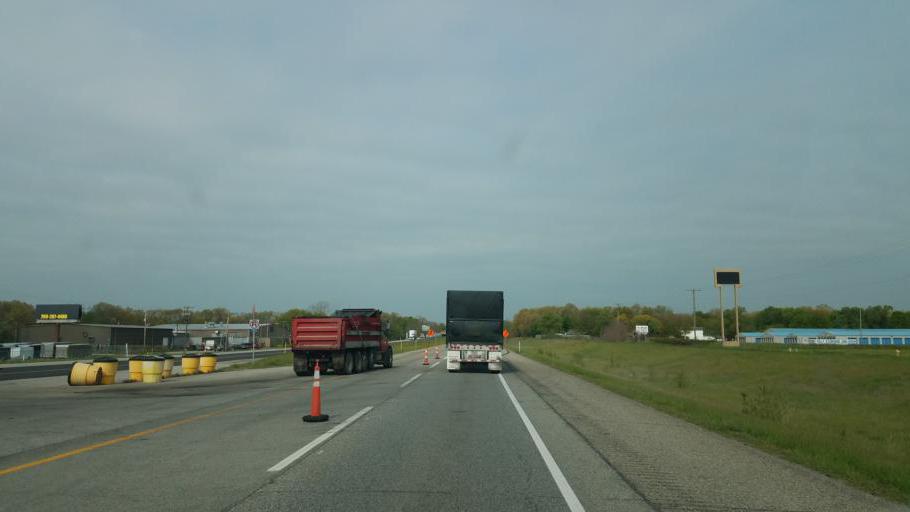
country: US
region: Indiana
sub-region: Elkhart County
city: Simonton Lake
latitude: 41.7312
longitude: -85.9765
